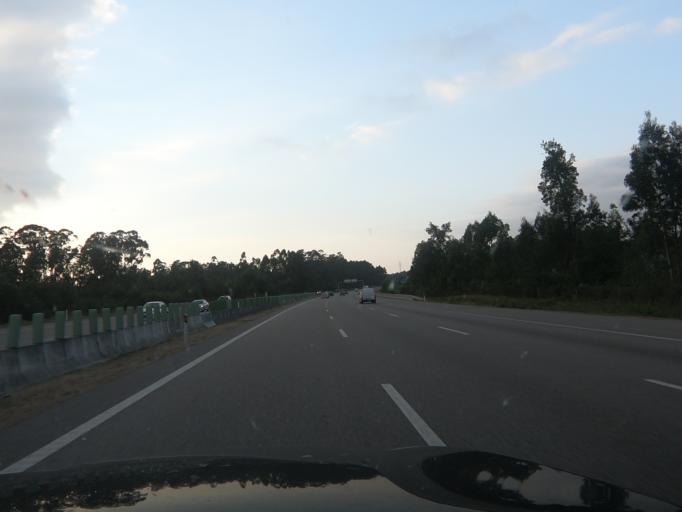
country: PT
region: Aveiro
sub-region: Estarreja
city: Beduido
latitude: 40.7898
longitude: -8.5484
